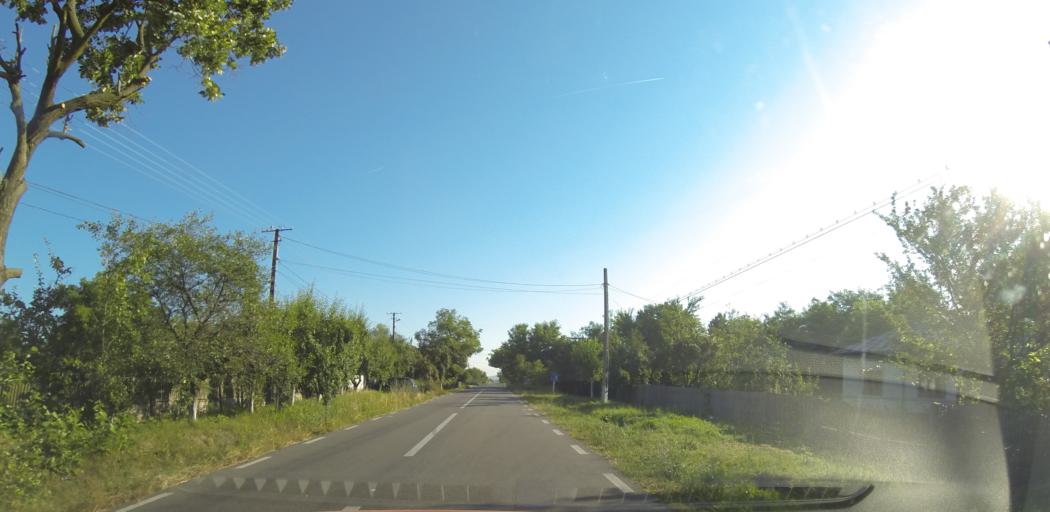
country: RO
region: Valcea
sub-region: Comuna Lacusteni
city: Lacusteni
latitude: 44.6981
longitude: 23.8985
